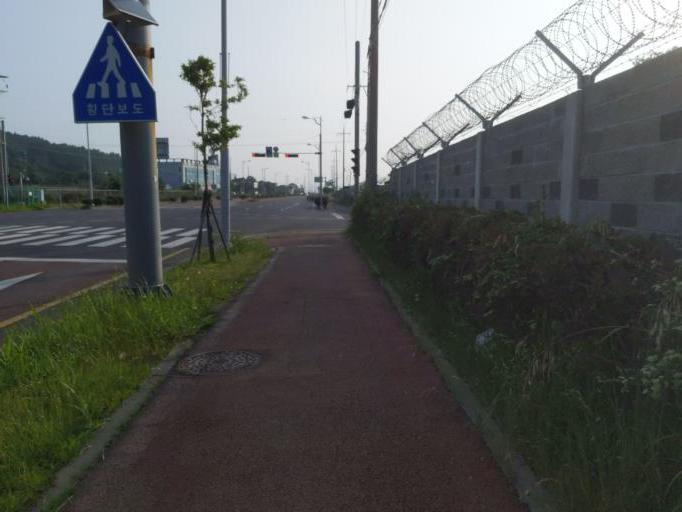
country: KR
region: Jeju-do
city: Gaigeturi
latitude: 33.2304
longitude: 126.2621
